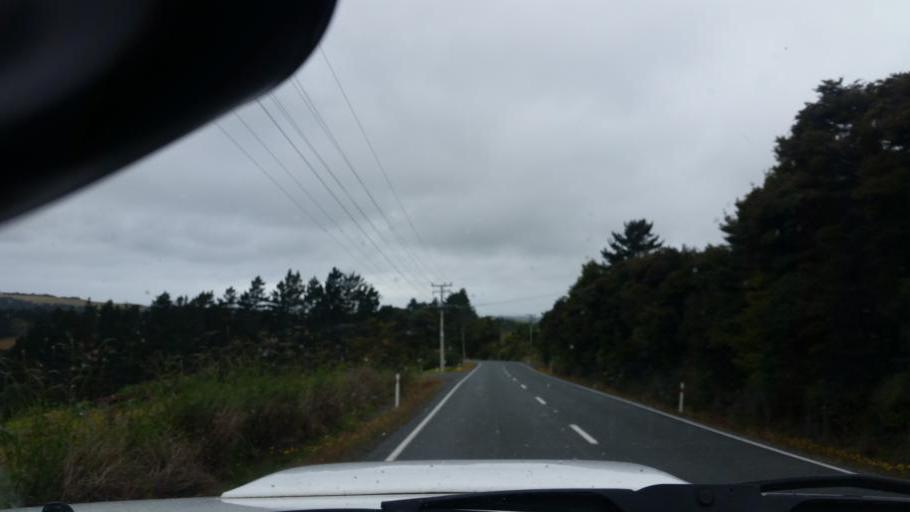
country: NZ
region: Auckland
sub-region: Auckland
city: Wellsford
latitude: -36.1324
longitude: 174.5420
